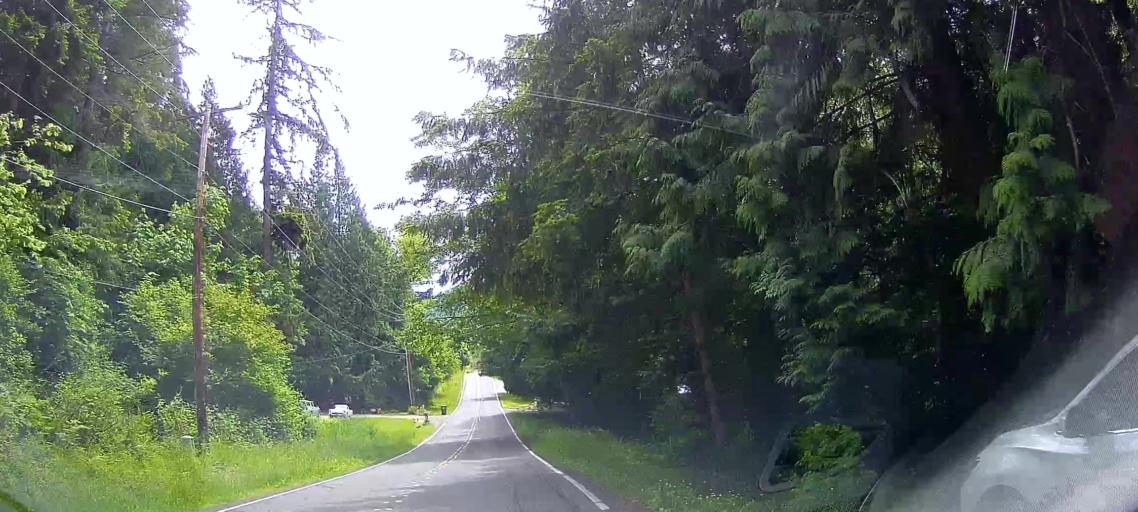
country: US
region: Washington
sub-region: Whatcom County
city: Bellingham
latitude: 48.7107
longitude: -122.4783
